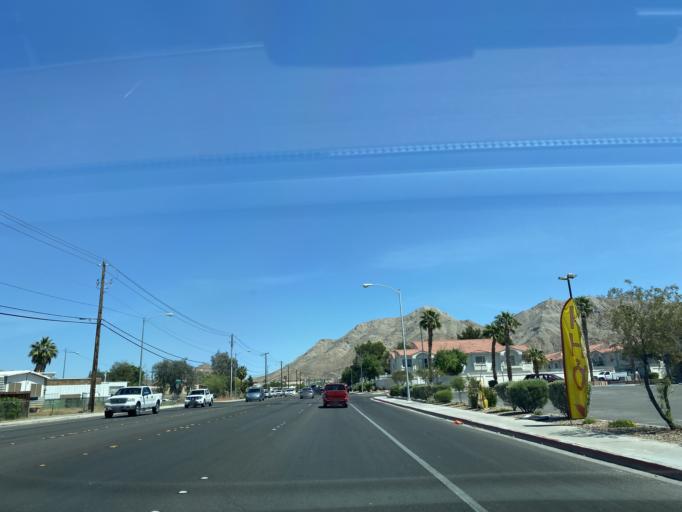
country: US
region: Nevada
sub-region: Clark County
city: Sunrise Manor
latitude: 36.1960
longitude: -115.0407
